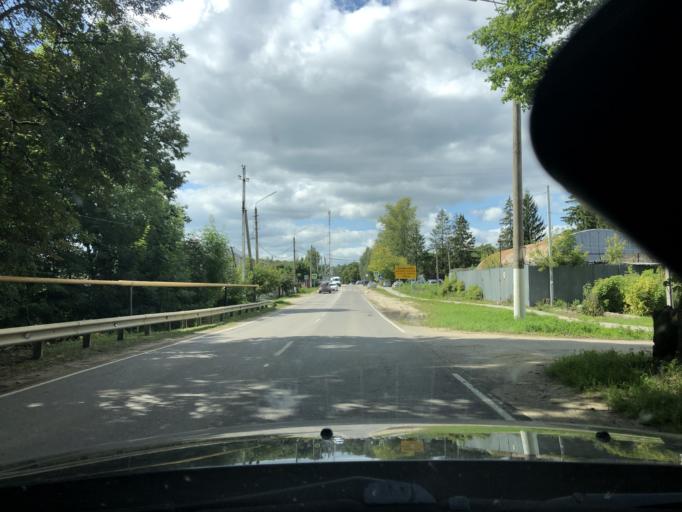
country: RU
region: Tula
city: Barsuki
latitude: 54.3383
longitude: 37.5525
